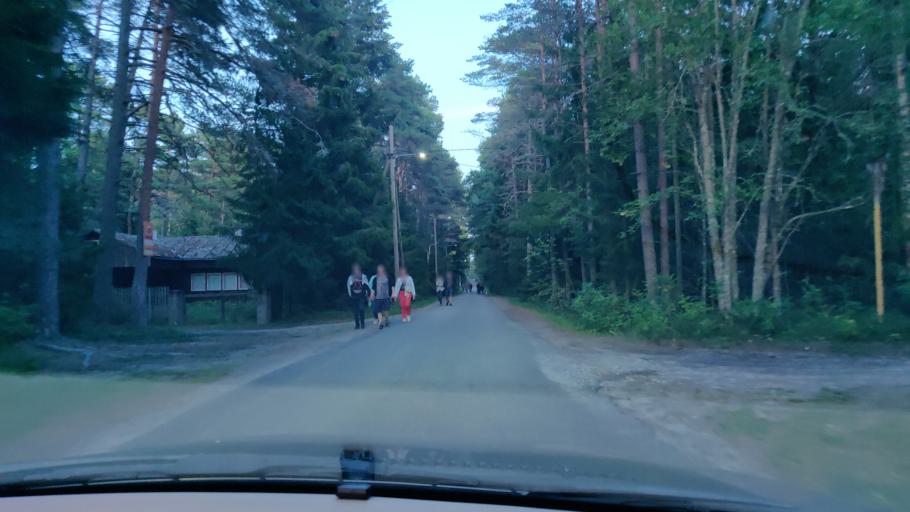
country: EE
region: Harju
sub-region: Keila linn
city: Keila
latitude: 59.3466
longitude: 24.2595
